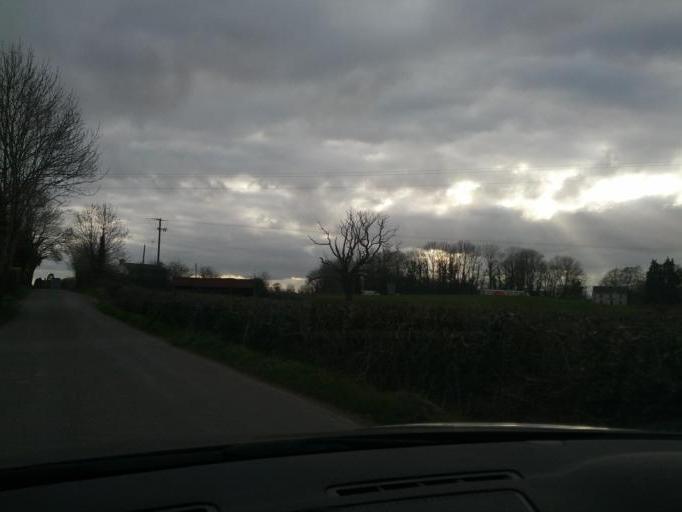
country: IE
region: Leinster
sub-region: Uibh Fhaili
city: Ferbane
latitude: 53.3620
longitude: -7.8481
